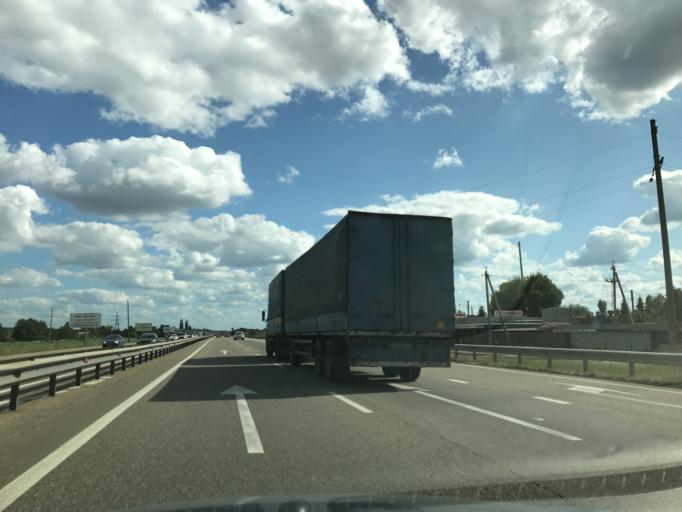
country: RU
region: Adygeya
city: Adygeysk
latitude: 44.9275
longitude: 39.1401
